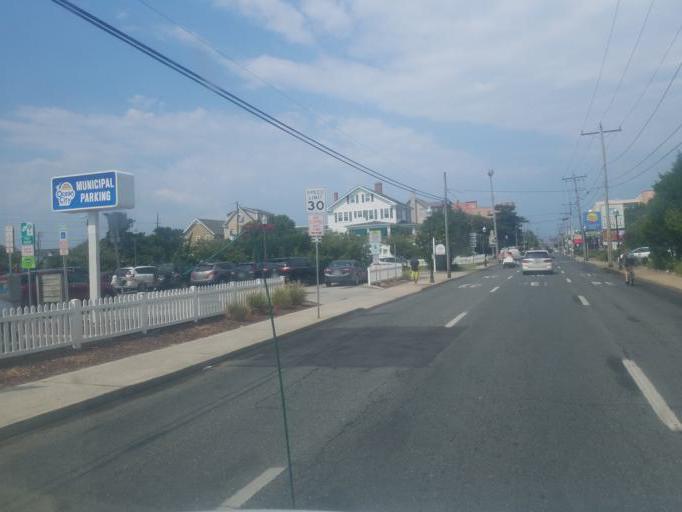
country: US
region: Maryland
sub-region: Worcester County
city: Ocean City
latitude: 38.3356
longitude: -75.0840
